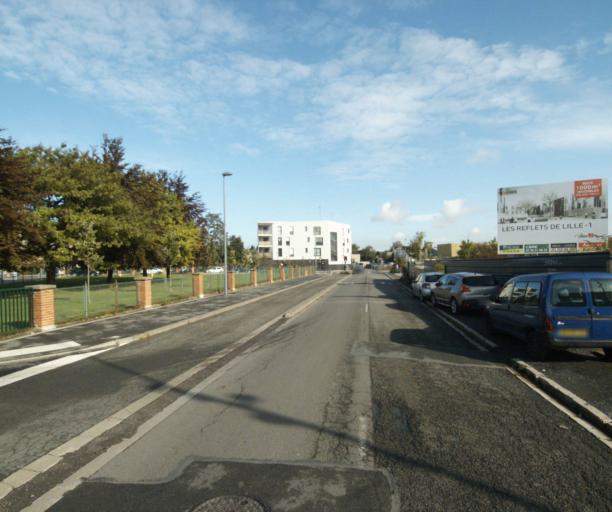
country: FR
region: Nord-Pas-de-Calais
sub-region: Departement du Nord
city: Loos
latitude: 50.6135
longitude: 3.0386
